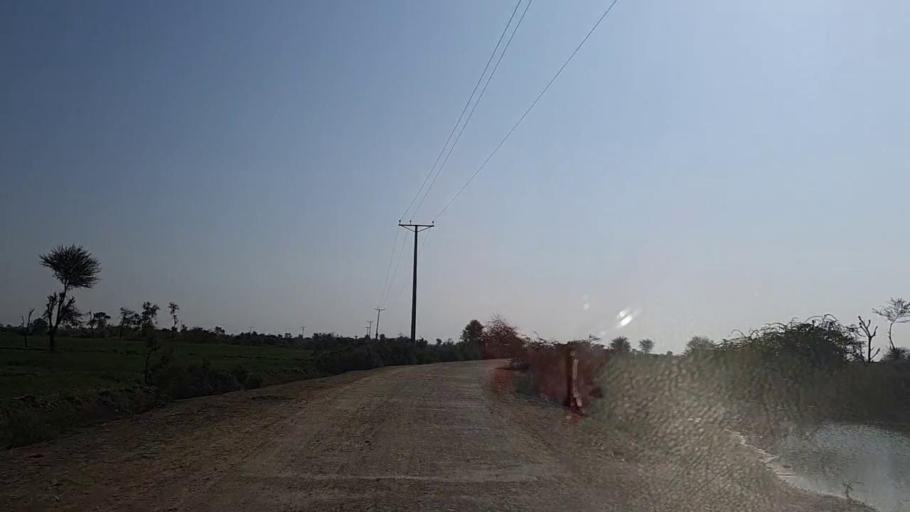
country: PK
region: Sindh
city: Sanghar
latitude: 26.0037
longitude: 69.0565
